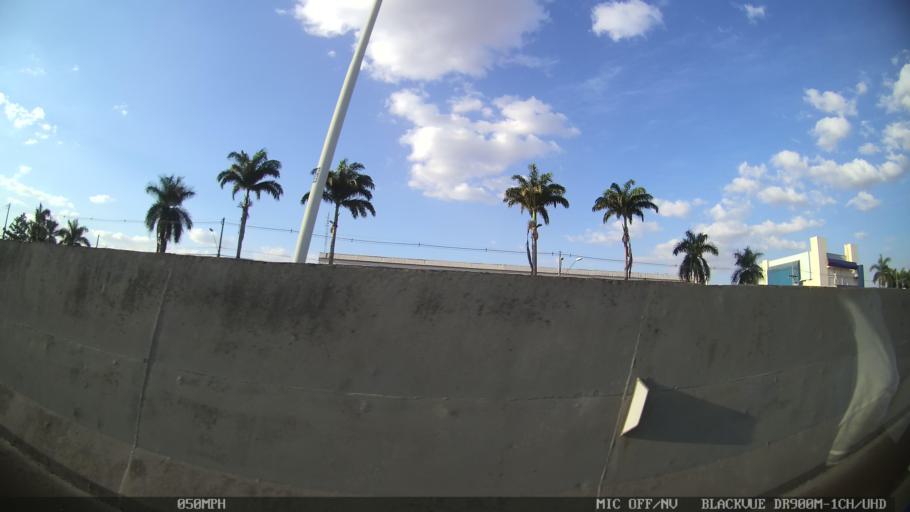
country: BR
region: Sao Paulo
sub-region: Ribeirao Preto
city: Ribeirao Preto
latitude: -21.1961
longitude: -47.7726
